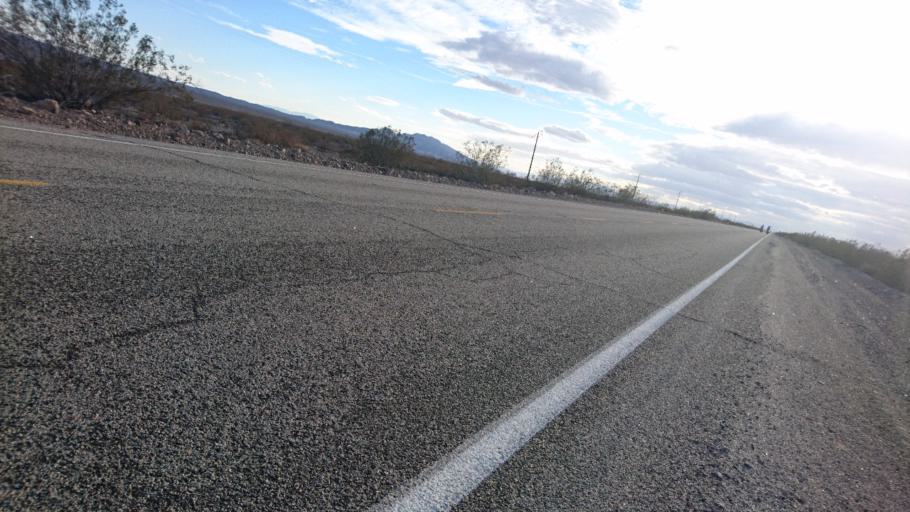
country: US
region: California
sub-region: San Bernardino County
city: Needles
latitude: 34.6740
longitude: -115.3352
